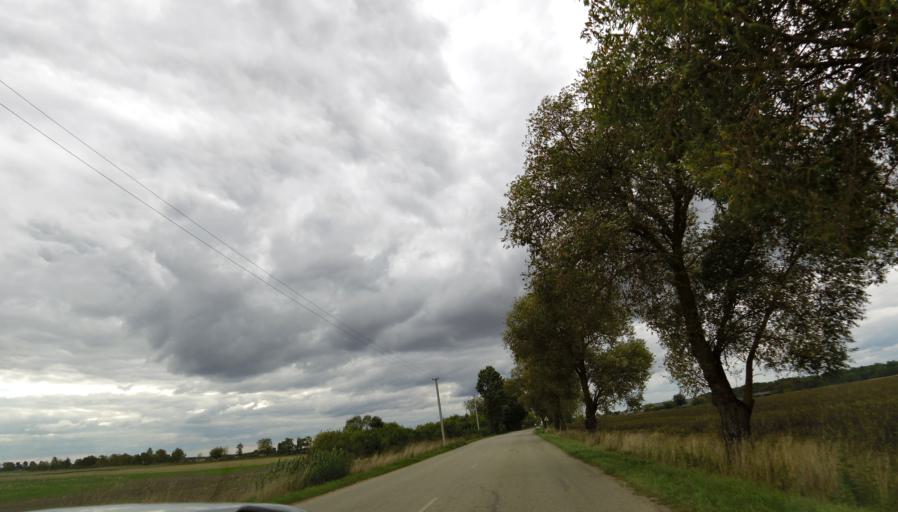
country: LT
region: Panevezys
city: Pasvalys
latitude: 56.0759
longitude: 24.3091
